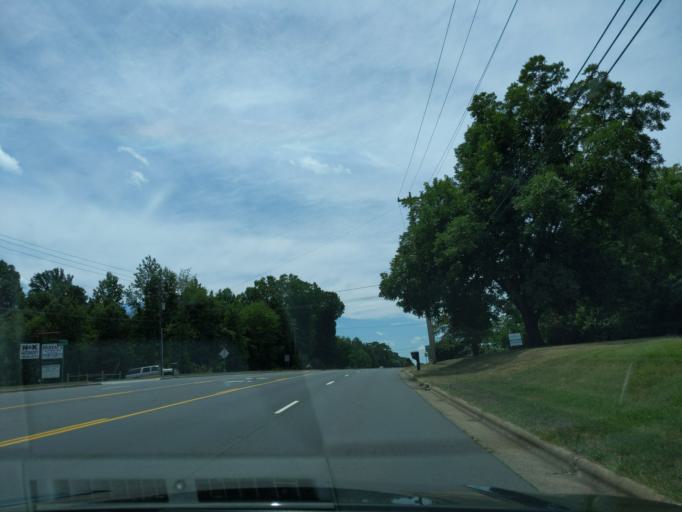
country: US
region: North Carolina
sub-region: Stanly County
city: Albemarle
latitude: 35.4078
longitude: -80.2021
